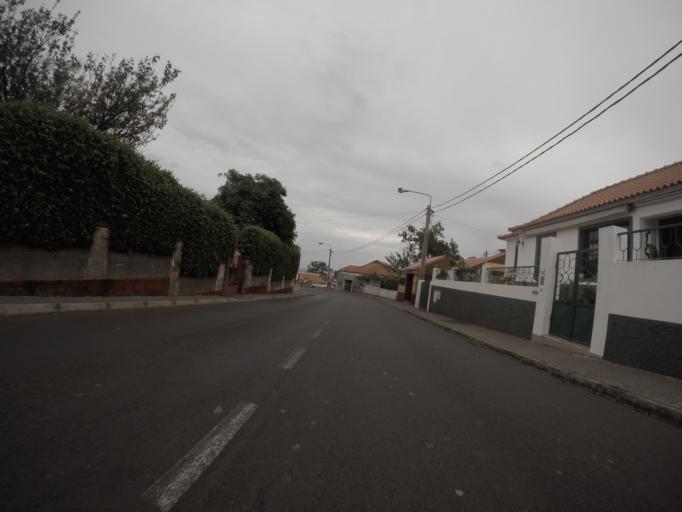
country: PT
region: Madeira
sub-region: Funchal
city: Nossa Senhora do Monte
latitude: 32.6576
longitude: -16.9207
